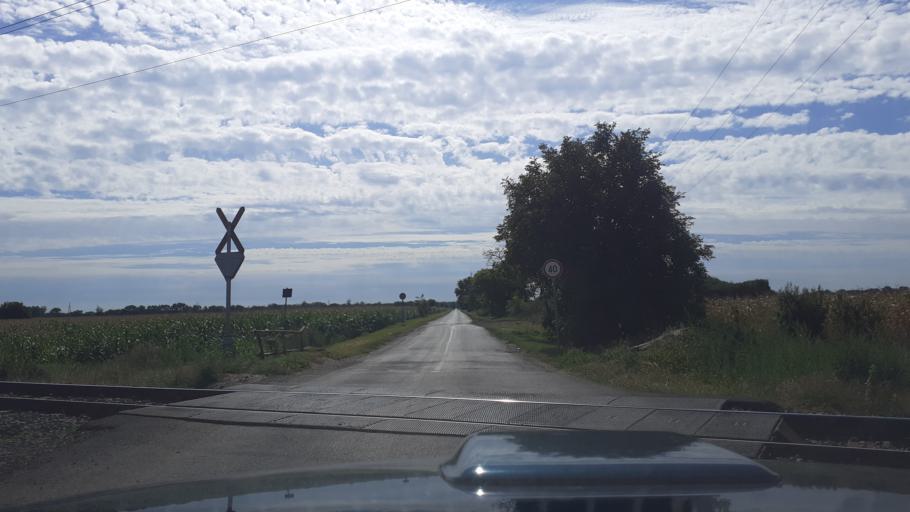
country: HU
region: Fejer
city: Pusztaszabolcs
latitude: 47.1289
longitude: 18.7661
